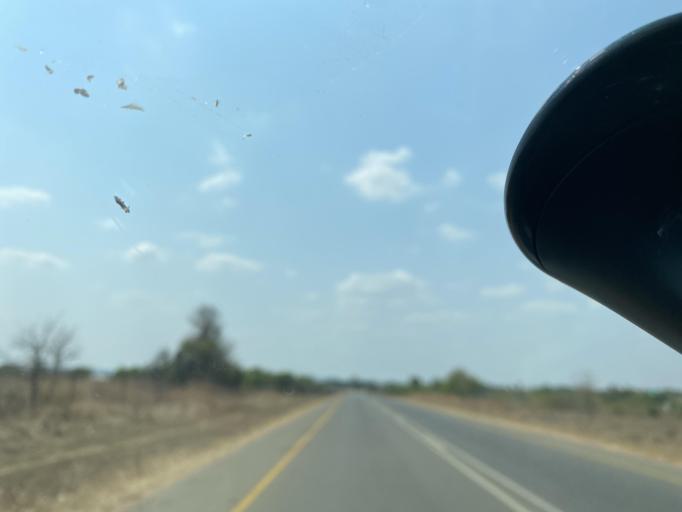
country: ZM
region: Lusaka
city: Chongwe
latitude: -15.5835
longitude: 28.7066
